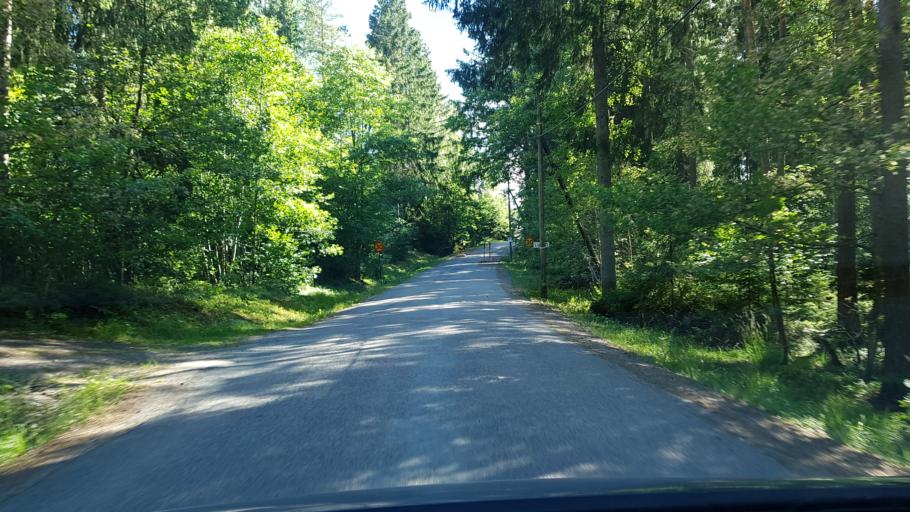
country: SE
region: Stockholm
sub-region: Upplands-Bro Kommun
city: Kungsaengen
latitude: 59.4990
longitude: 17.8079
